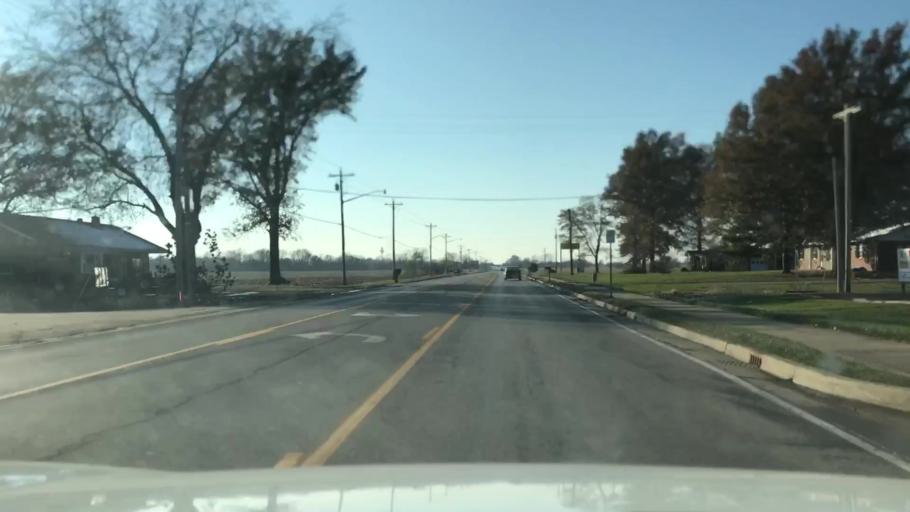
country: US
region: Illinois
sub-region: Clinton County
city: New Baden
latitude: 38.5352
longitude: -89.7110
